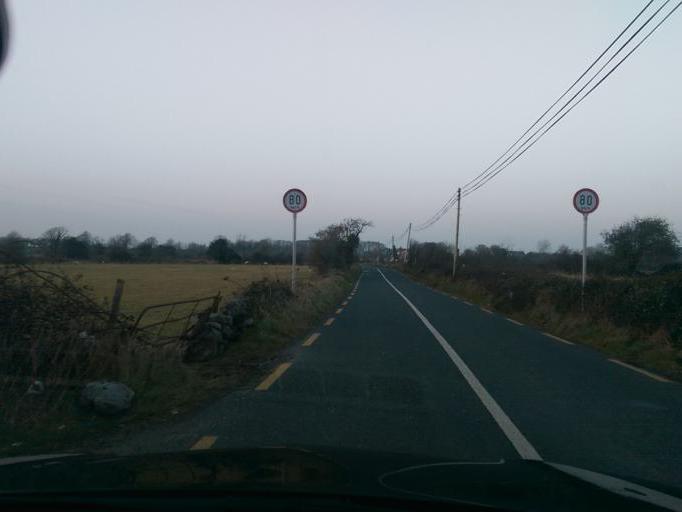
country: IE
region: Connaught
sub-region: County Galway
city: Loughrea
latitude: 53.2090
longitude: -8.5998
